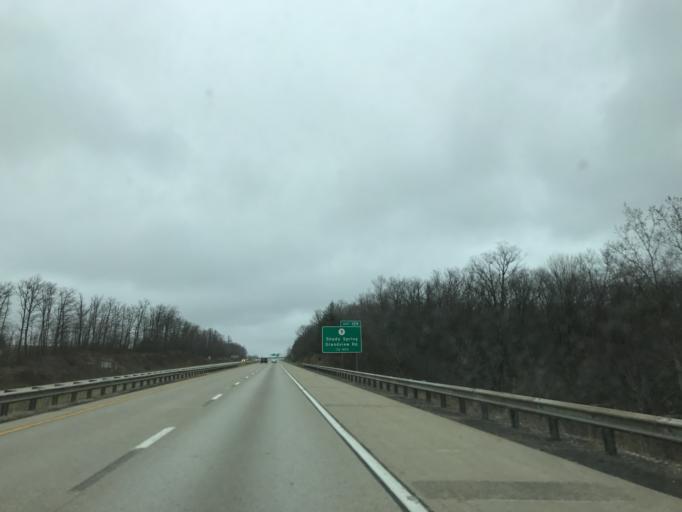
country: US
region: West Virginia
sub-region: Raleigh County
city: Daniels
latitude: 37.7736
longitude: -81.0825
